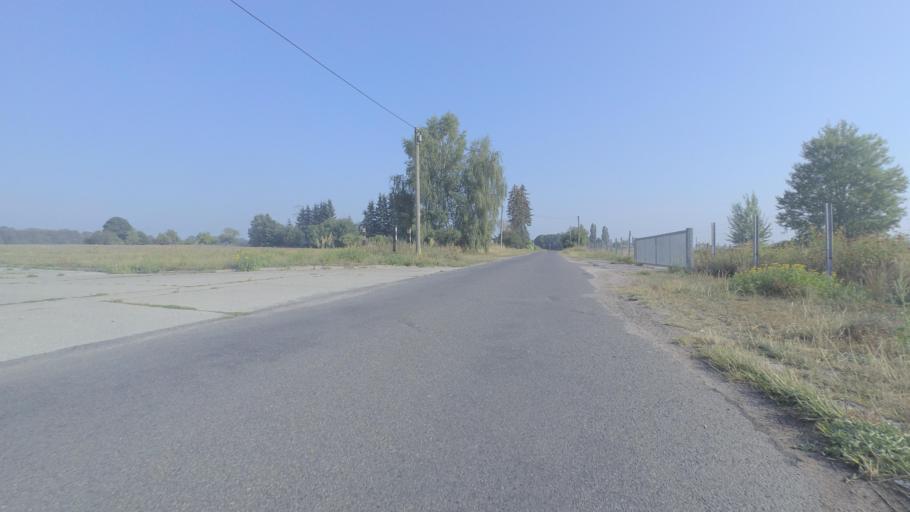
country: DE
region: Mecklenburg-Vorpommern
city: Malchow
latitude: 53.3606
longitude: 12.3812
